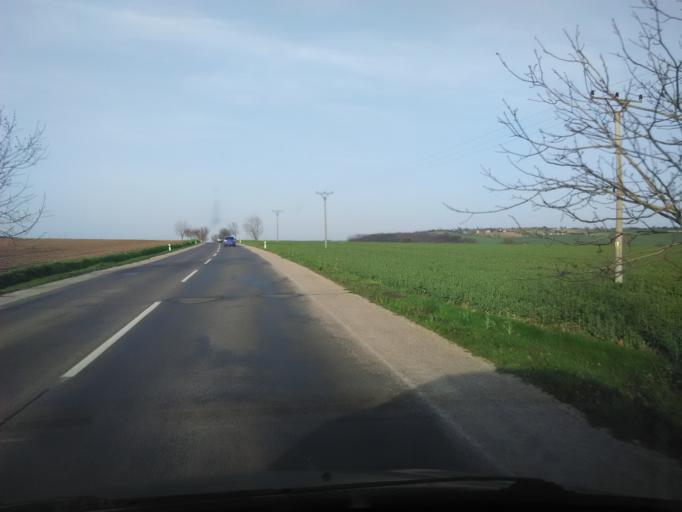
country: SK
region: Nitriansky
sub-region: Okres Nitra
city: Vrable
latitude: 48.1079
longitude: 18.3429
